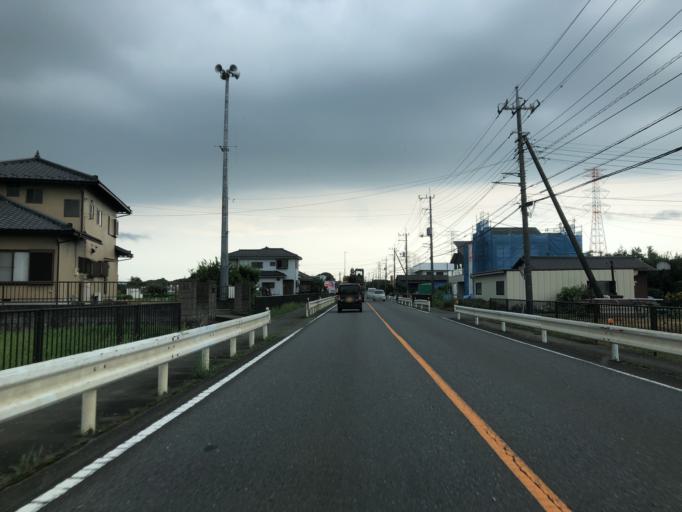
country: JP
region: Saitama
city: Sakado
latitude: 36.0232
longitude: 139.3954
